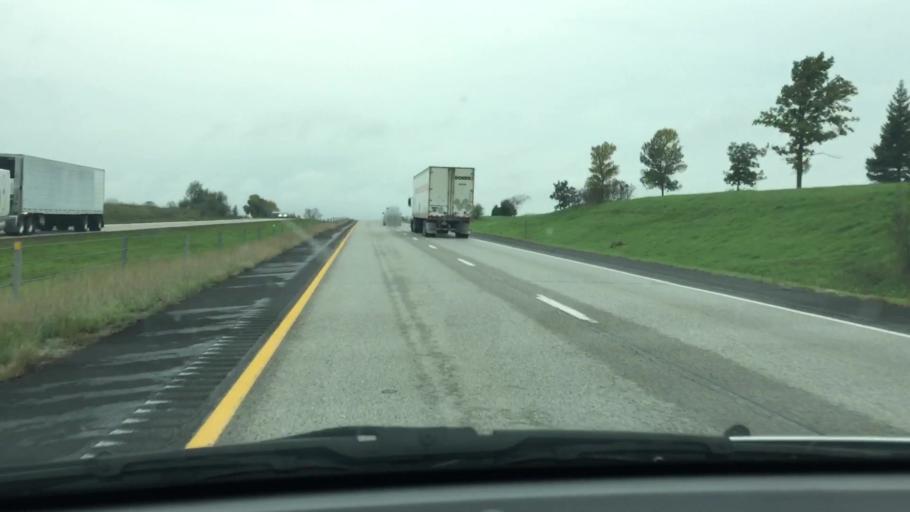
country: US
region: Iowa
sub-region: Johnson County
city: Tiffin
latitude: 41.6943
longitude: -91.7423
